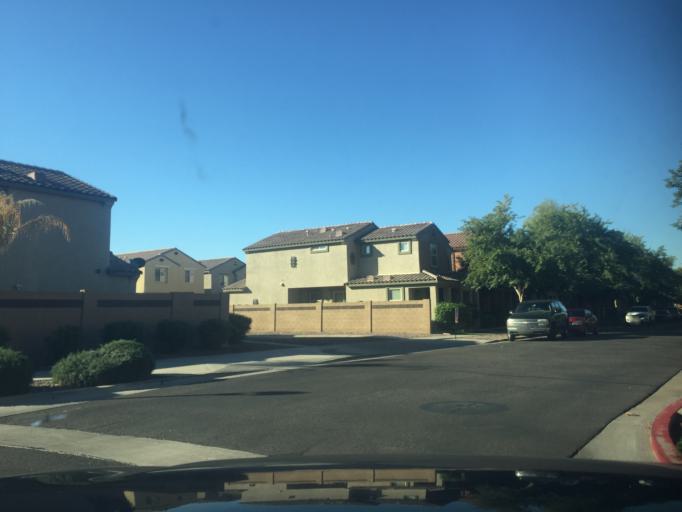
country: US
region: Arizona
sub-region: Maricopa County
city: Tolleson
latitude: 33.4719
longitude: -112.2254
